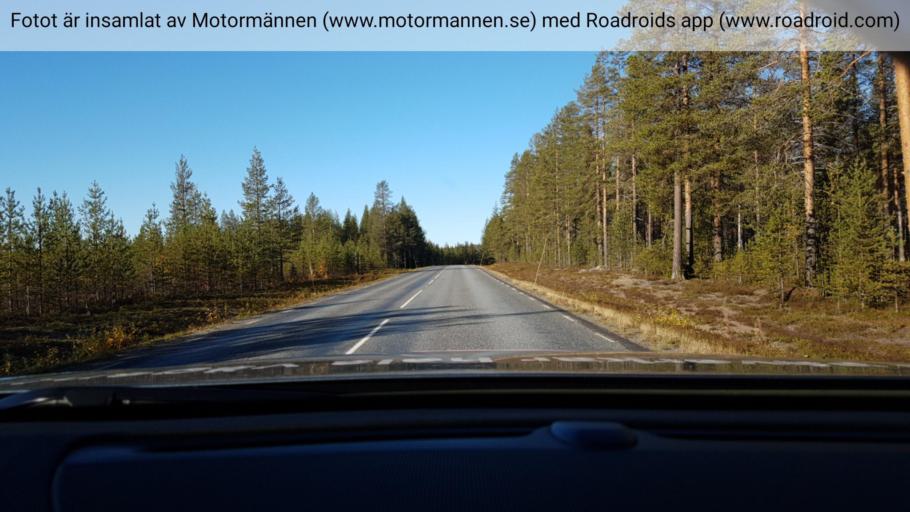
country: SE
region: Vaesterbotten
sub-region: Skelleftea Kommun
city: Boliden
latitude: 65.3820
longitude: 20.1482
